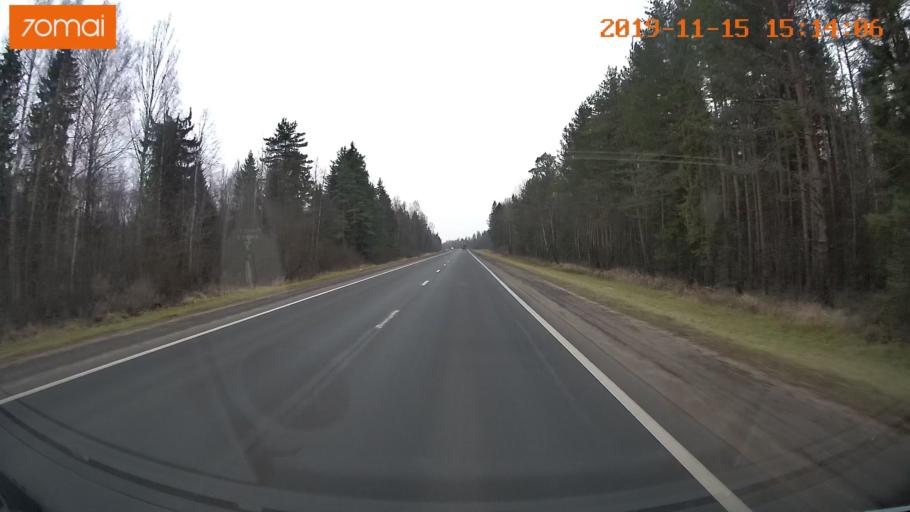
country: RU
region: Jaroslavl
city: Danilov
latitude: 58.3046
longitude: 40.2096
